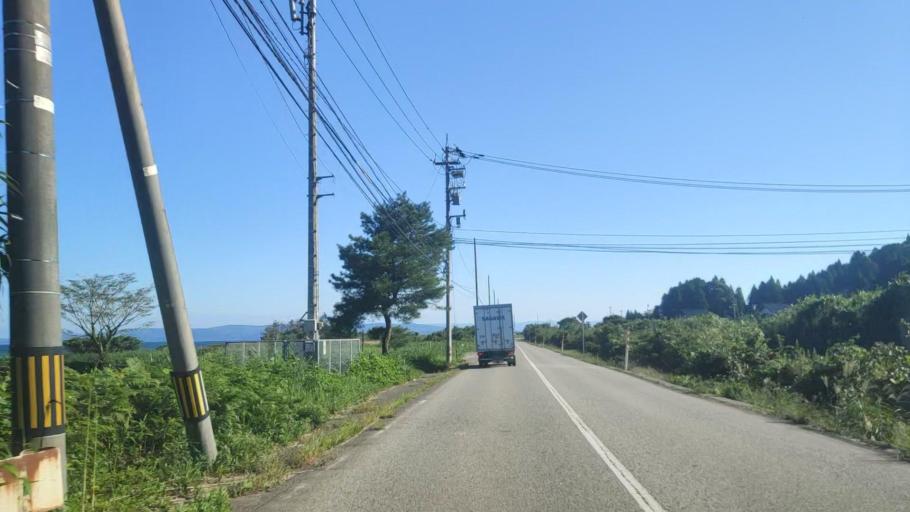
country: JP
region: Ishikawa
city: Nanao
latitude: 37.1979
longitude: 136.9099
